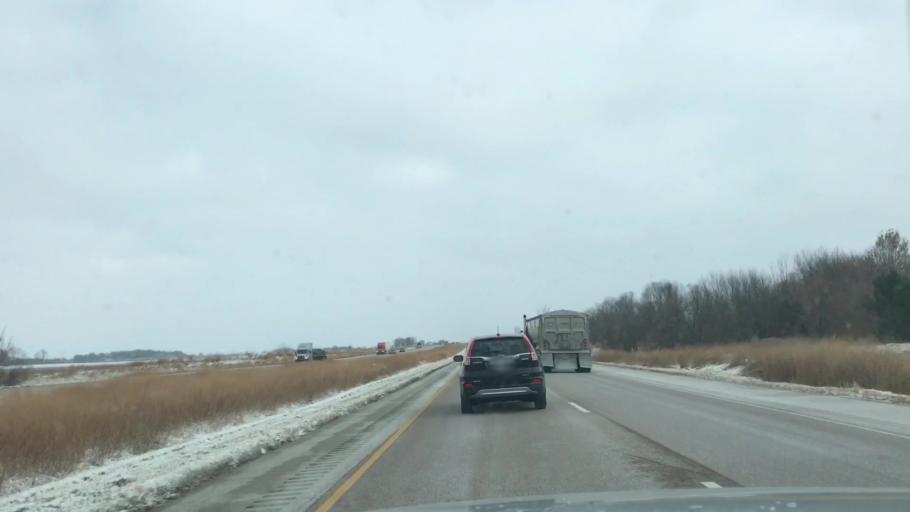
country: US
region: Illinois
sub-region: Macoupin County
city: Mount Olive
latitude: 39.1322
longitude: -89.7112
